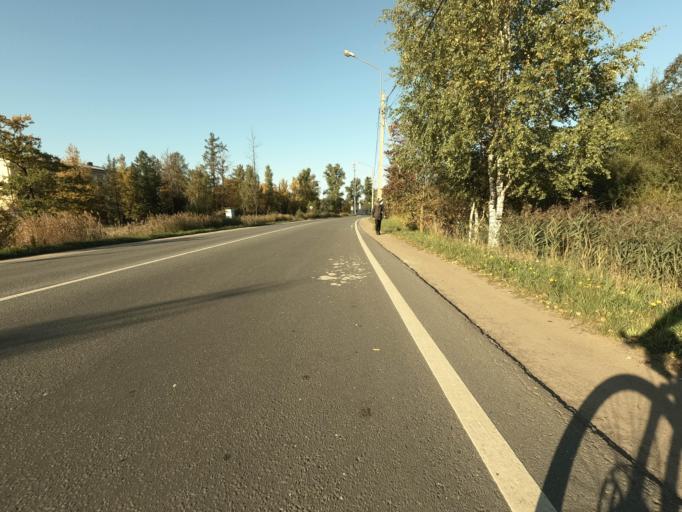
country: RU
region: St.-Petersburg
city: Kolpino
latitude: 59.7554
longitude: 30.6161
